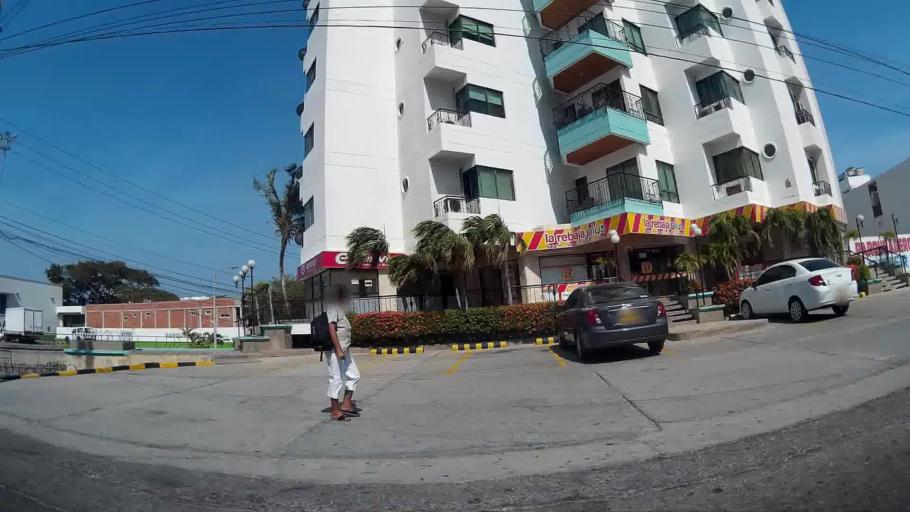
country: CO
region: Magdalena
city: Santa Marta
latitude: 11.1951
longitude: -74.2259
